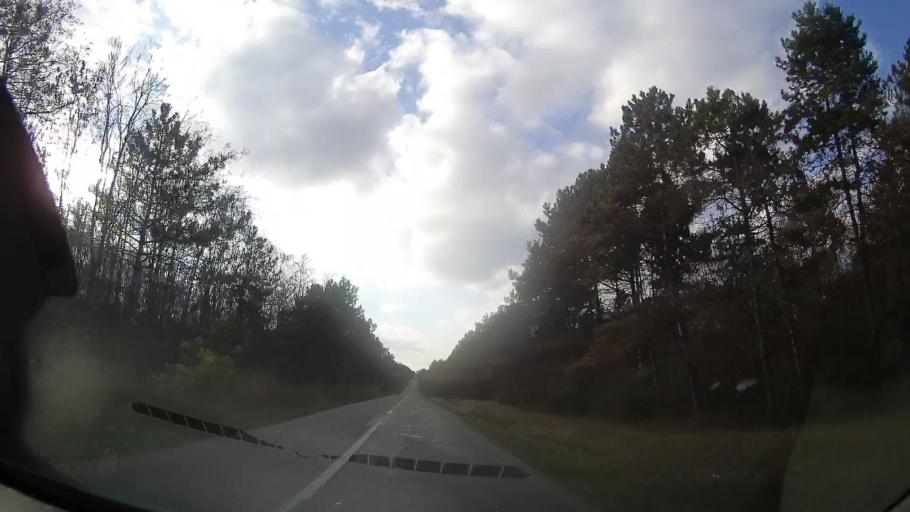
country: RO
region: Constanta
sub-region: Comuna Negru Voda
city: Negru Voda
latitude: 43.8193
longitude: 28.2703
